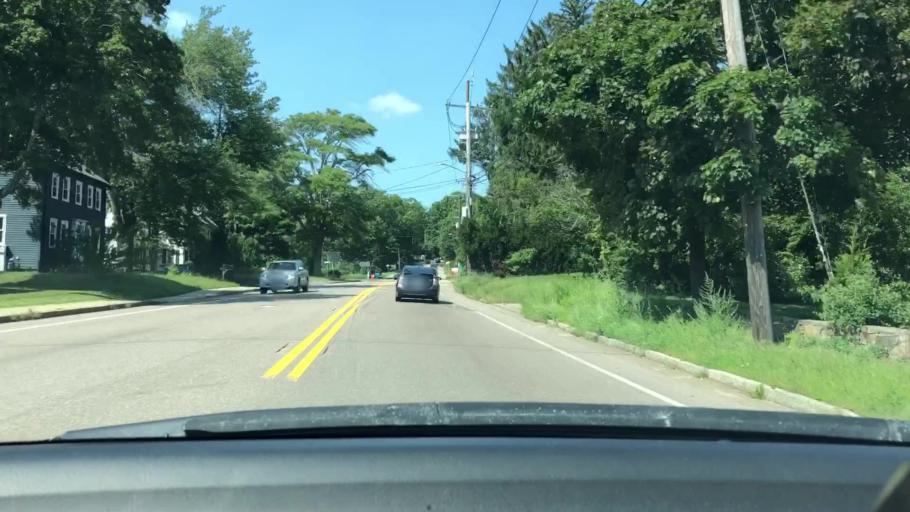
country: US
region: Massachusetts
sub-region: Norfolk County
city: Canton
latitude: 42.1922
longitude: -71.1179
